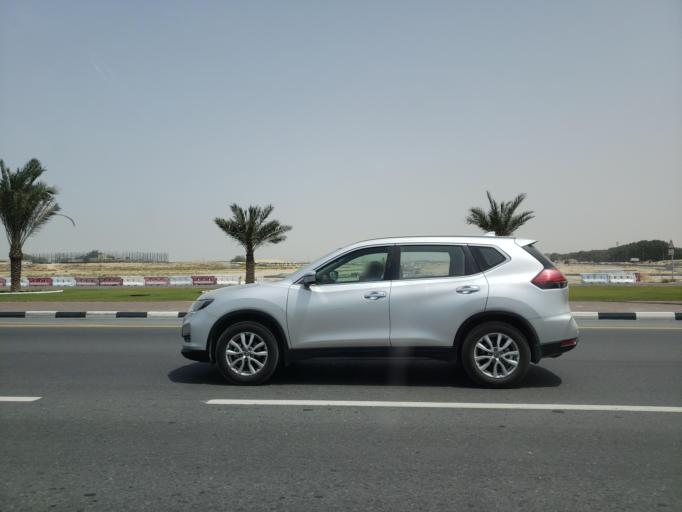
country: AE
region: Ash Shariqah
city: Sharjah
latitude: 25.3314
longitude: 55.4713
